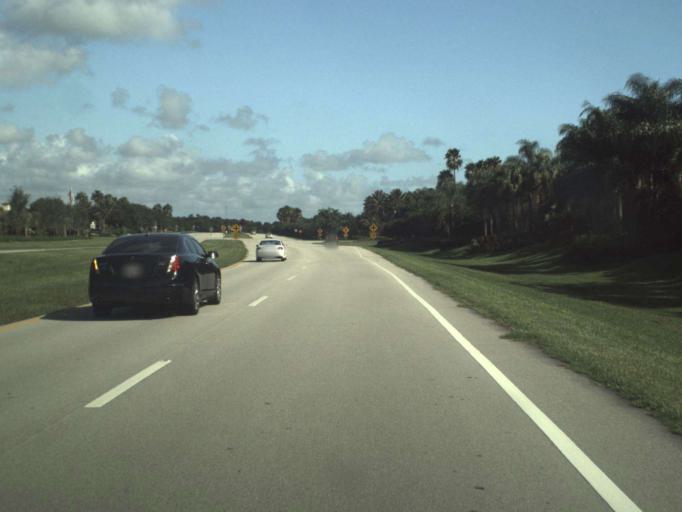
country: US
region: Florida
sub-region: Indian River County
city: Gifford
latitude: 27.6816
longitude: -80.4035
